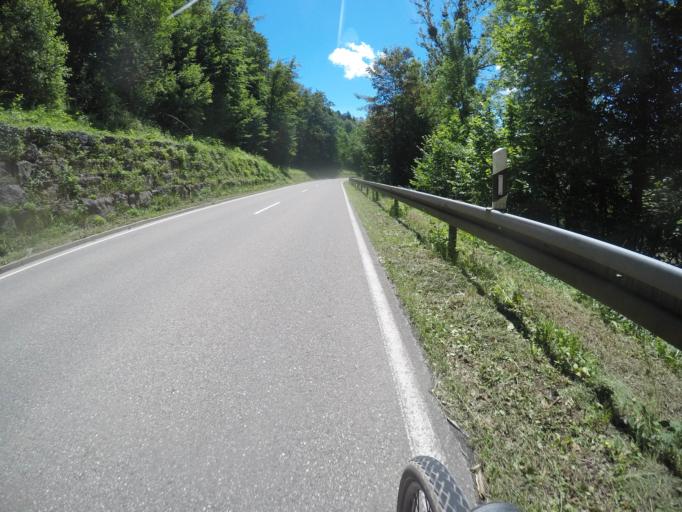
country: DE
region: Baden-Wuerttemberg
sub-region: Tuebingen Region
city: Hirrlingen
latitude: 48.4474
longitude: 8.8361
